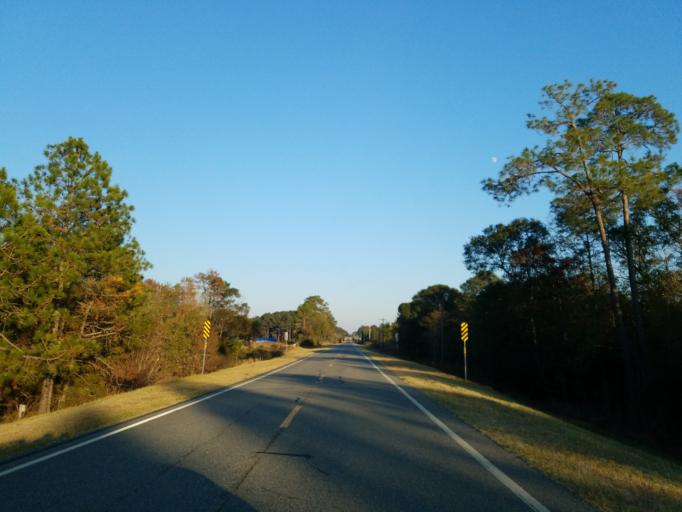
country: US
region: Georgia
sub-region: Turner County
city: Ashburn
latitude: 31.8596
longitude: -83.6401
